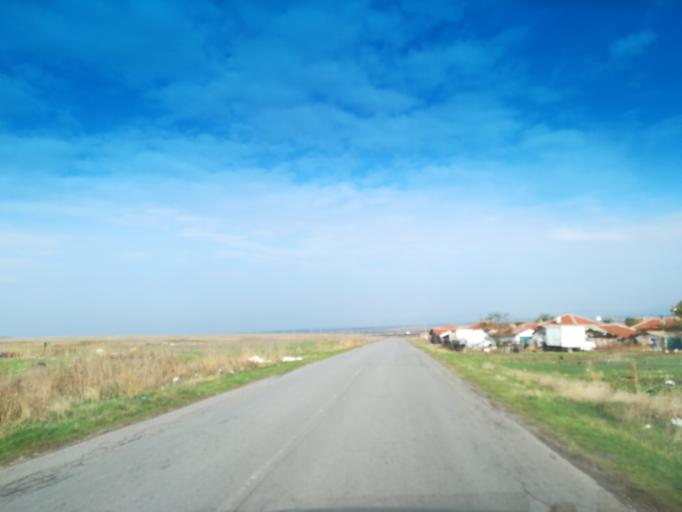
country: BG
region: Stara Zagora
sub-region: Obshtina Chirpan
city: Chirpan
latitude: 42.2003
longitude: 25.3101
